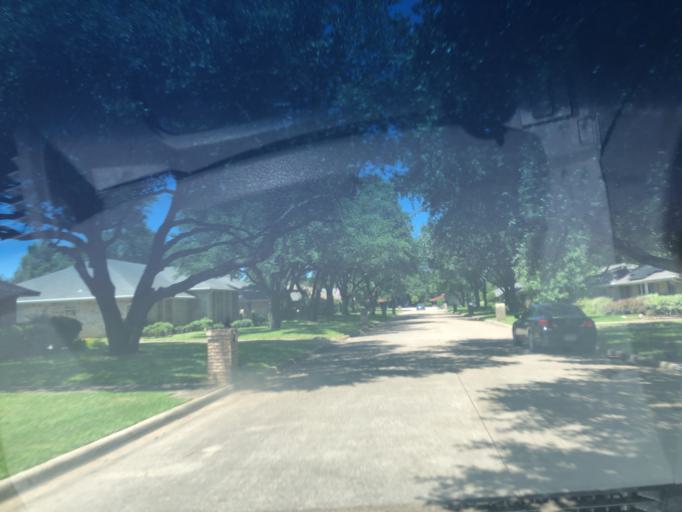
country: US
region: Texas
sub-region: Dallas County
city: Grand Prairie
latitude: 32.7787
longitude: -97.0413
